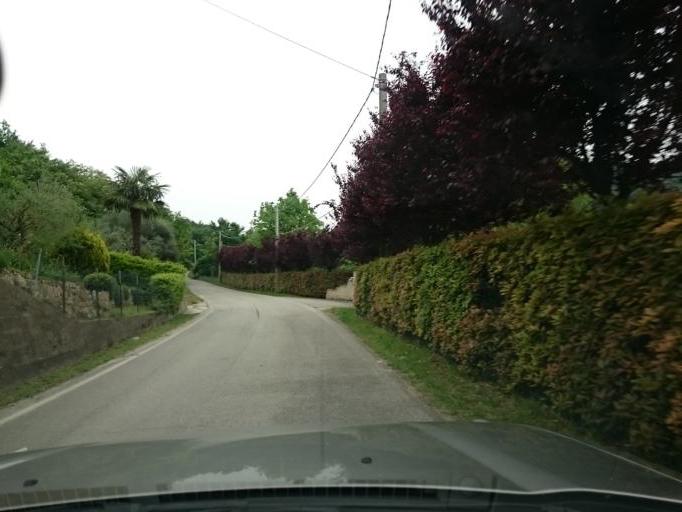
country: IT
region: Veneto
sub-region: Provincia di Padova
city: Montegrotto Terme
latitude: 45.3165
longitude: 11.7677
